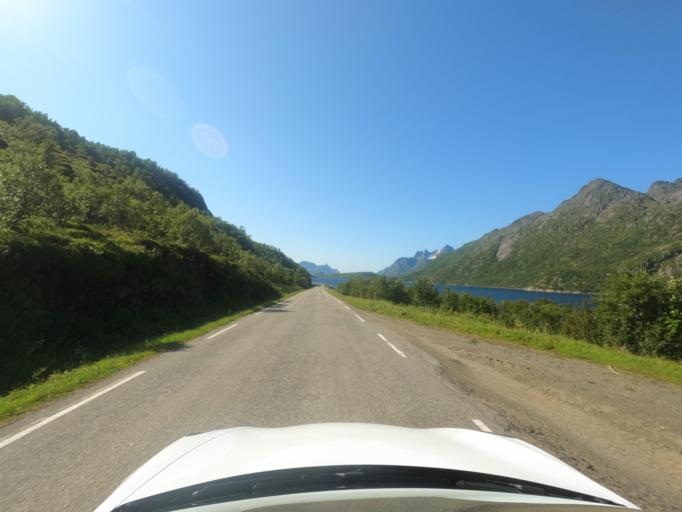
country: NO
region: Nordland
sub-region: Hadsel
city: Stokmarknes
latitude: 68.3864
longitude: 15.0934
